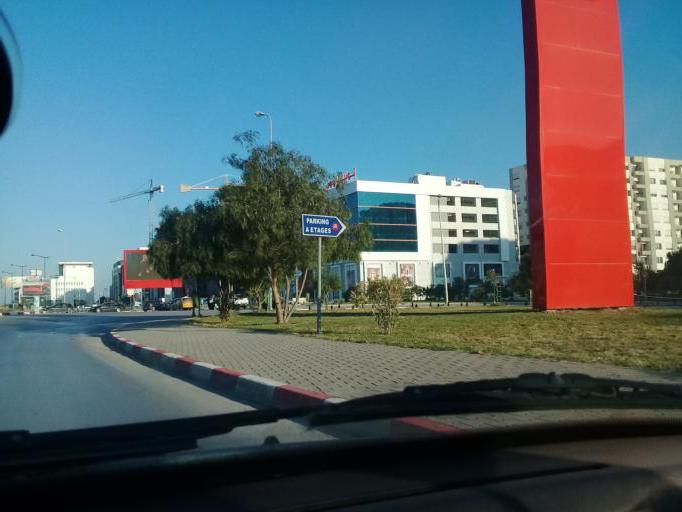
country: TN
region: Tunis
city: La Goulette
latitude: 36.8482
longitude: 10.2797
